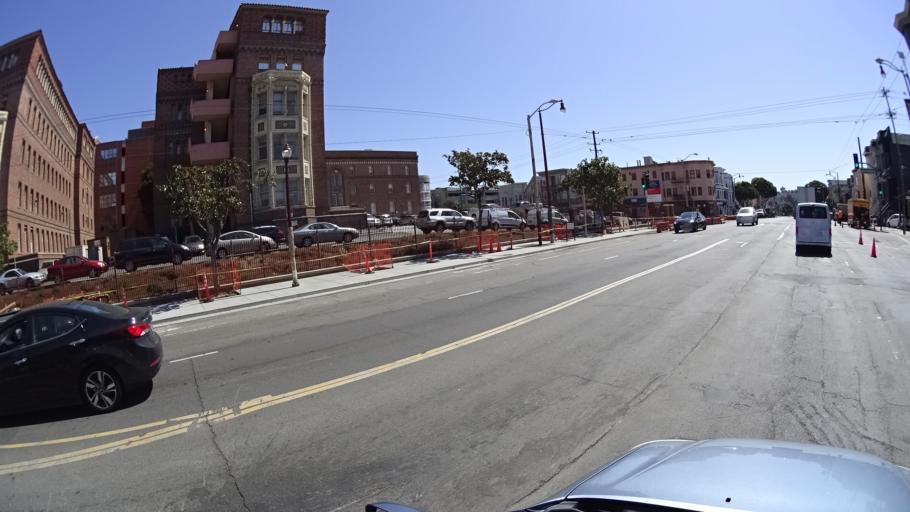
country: US
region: California
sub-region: San Francisco County
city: San Francisco
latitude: 37.7549
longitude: -122.4066
